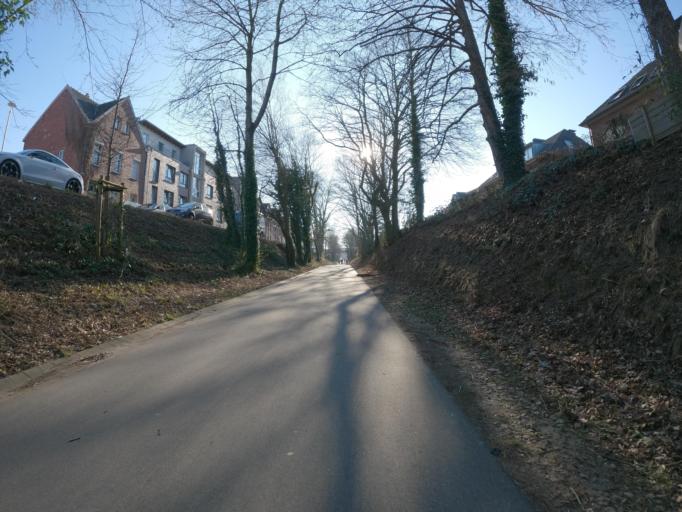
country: DE
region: North Rhine-Westphalia
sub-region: Regierungsbezirk Koln
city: Wurselen
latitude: 50.8207
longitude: 6.1379
